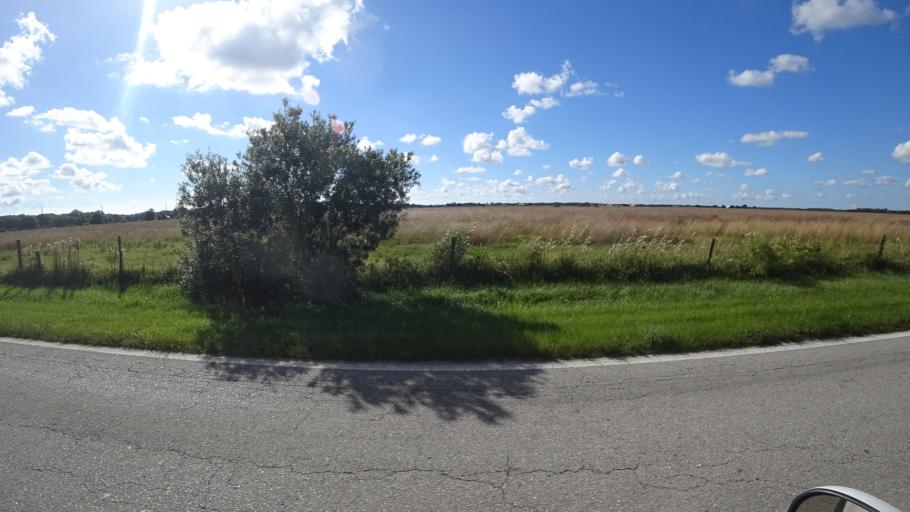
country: US
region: Florida
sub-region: Sarasota County
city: Lake Sarasota
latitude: 27.3360
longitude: -82.2694
